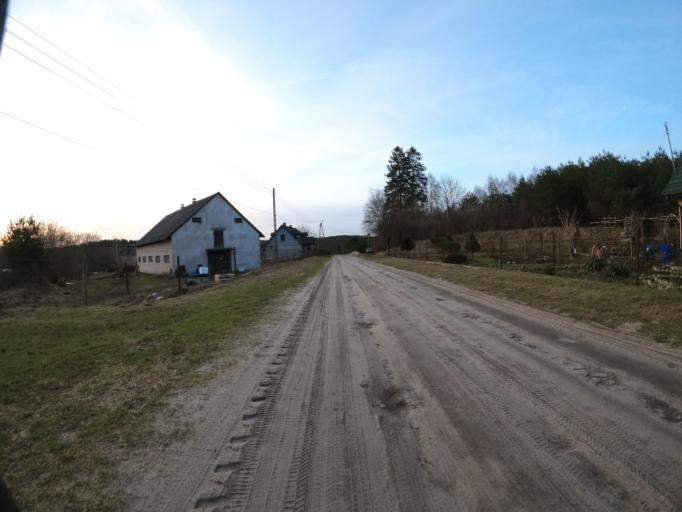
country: PL
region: West Pomeranian Voivodeship
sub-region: Powiat koszalinski
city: Polanow
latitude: 54.1988
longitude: 16.7169
